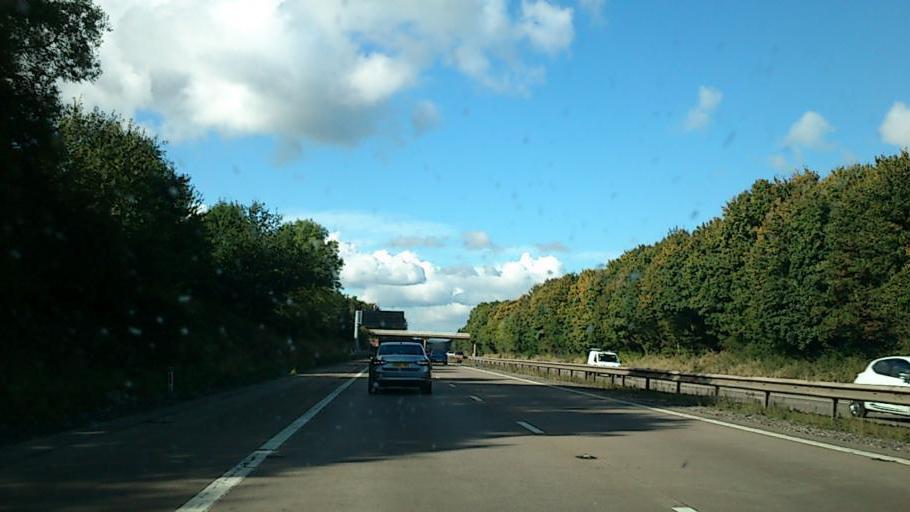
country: GB
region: England
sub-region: Shropshire
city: Albrighton
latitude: 52.6532
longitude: -2.2715
